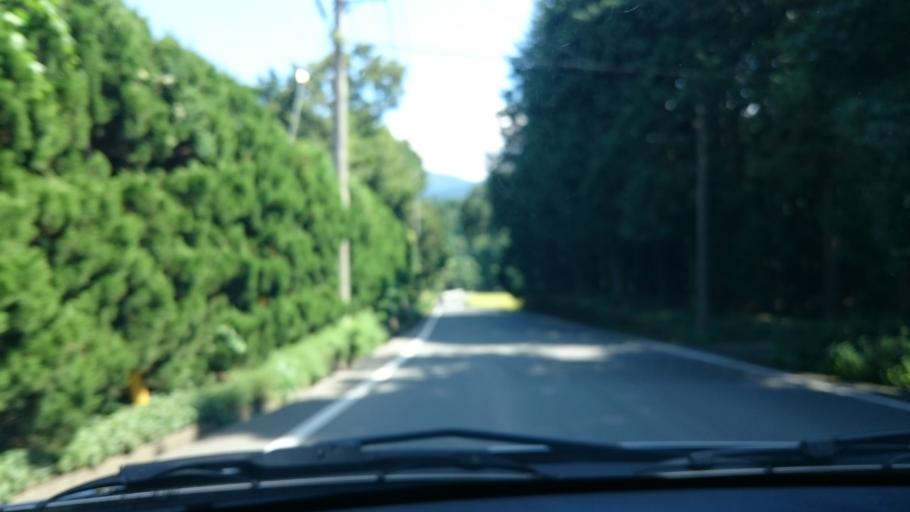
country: JP
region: Shizuoka
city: Gotemba
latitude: 35.2815
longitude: 138.9308
